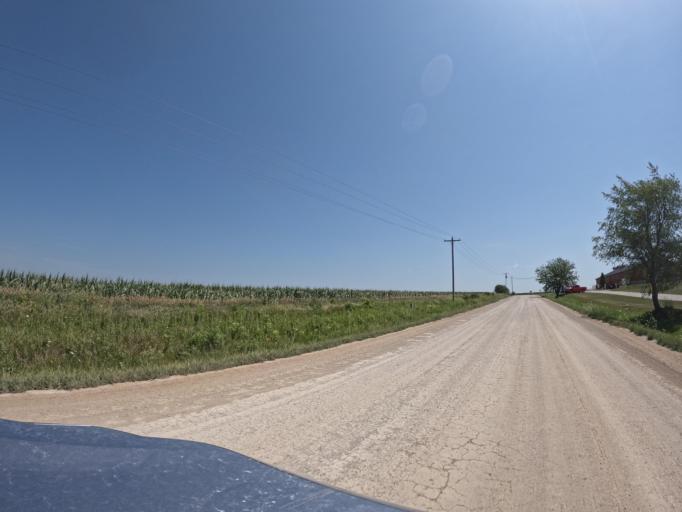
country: US
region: Iowa
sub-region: Henry County
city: Mount Pleasant
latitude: 40.9375
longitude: -91.5180
